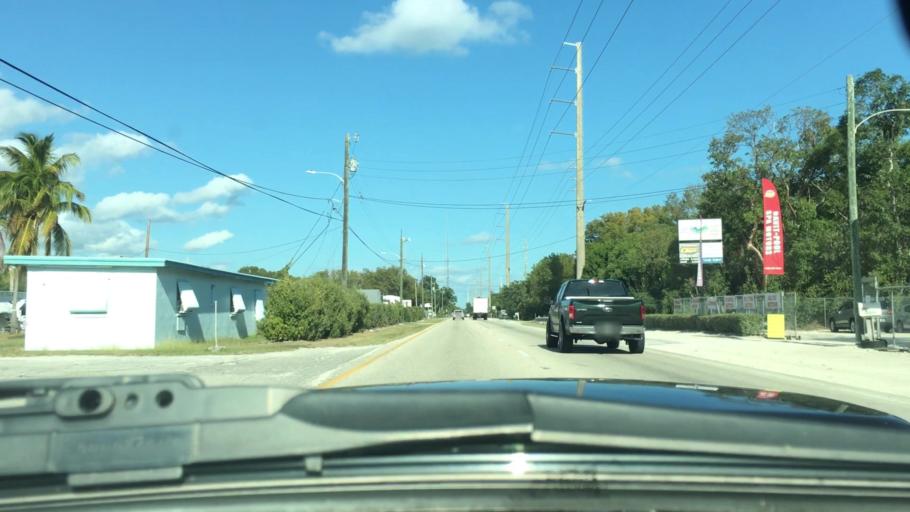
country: US
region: Florida
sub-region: Monroe County
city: Key Largo
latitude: 25.0840
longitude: -80.4517
